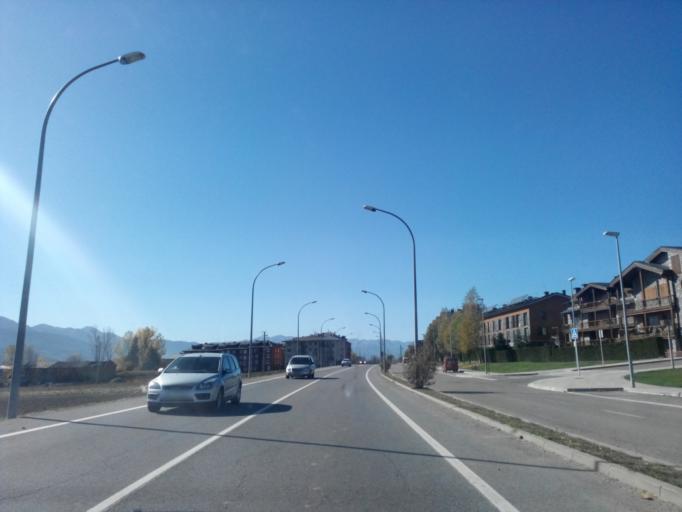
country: ES
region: Catalonia
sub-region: Provincia de Girona
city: Puigcerda
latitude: 42.4292
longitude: 1.9323
